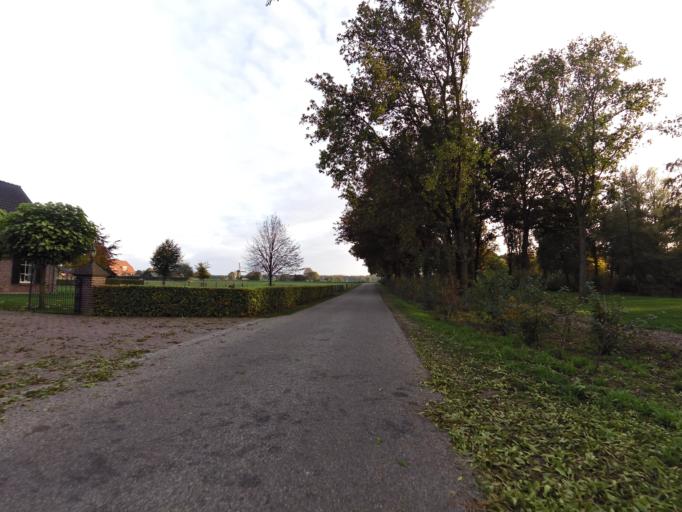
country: NL
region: Gelderland
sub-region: Gemeente Doesburg
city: Doesburg
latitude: 51.9708
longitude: 6.1787
